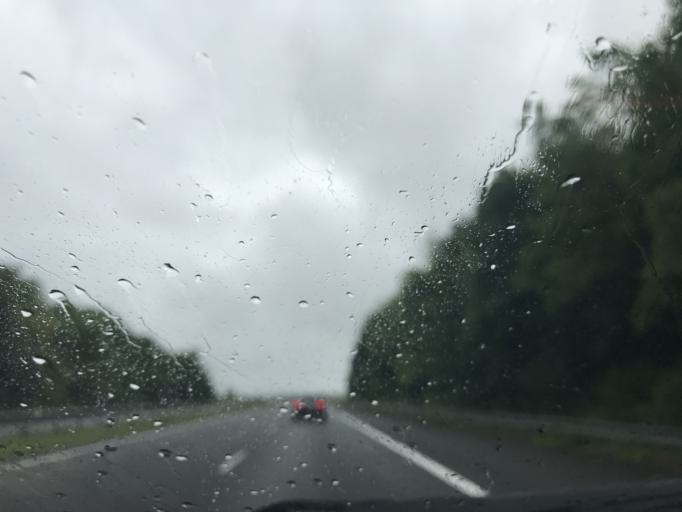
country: FR
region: Centre
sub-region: Departement du Cher
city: Mehun-sur-Yevre
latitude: 47.1457
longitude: 2.1856
